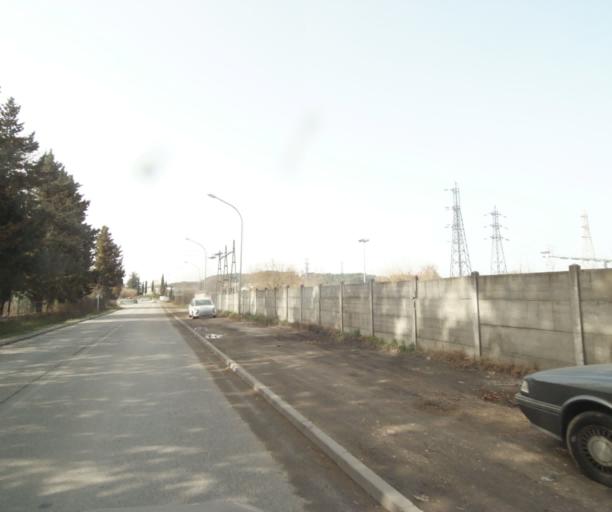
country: FR
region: Provence-Alpes-Cote d'Azur
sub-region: Departement des Bouches-du-Rhone
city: Gardanne
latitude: 43.4652
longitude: 5.4880
